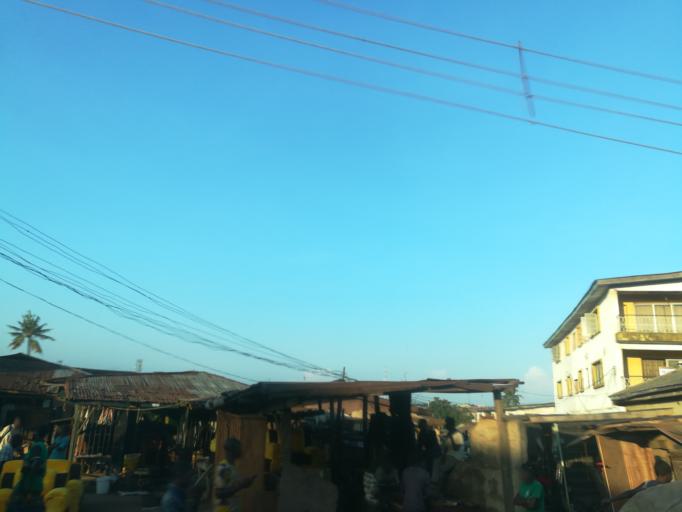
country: NG
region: Lagos
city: Ikorodu
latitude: 6.6180
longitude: 3.5082
